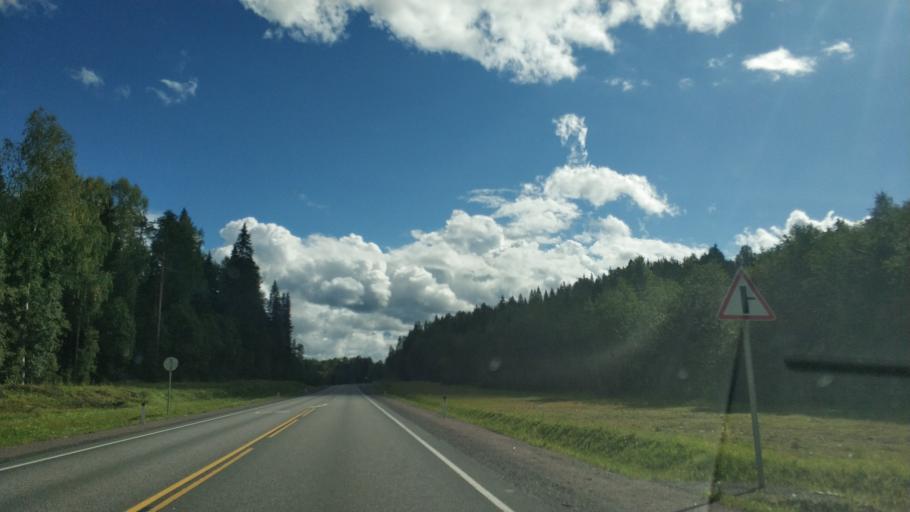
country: RU
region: Republic of Karelia
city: Ruskeala
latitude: 61.9099
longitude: 30.6285
